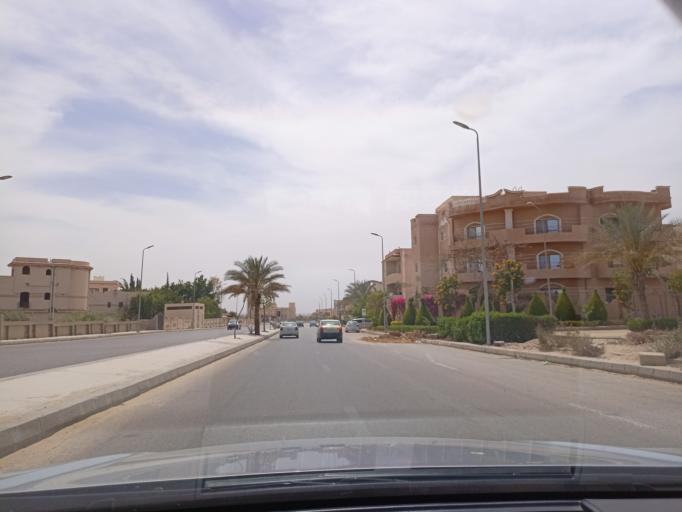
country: EG
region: Muhafazat al Qalyubiyah
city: Al Khankah
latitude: 30.2363
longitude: 31.4961
